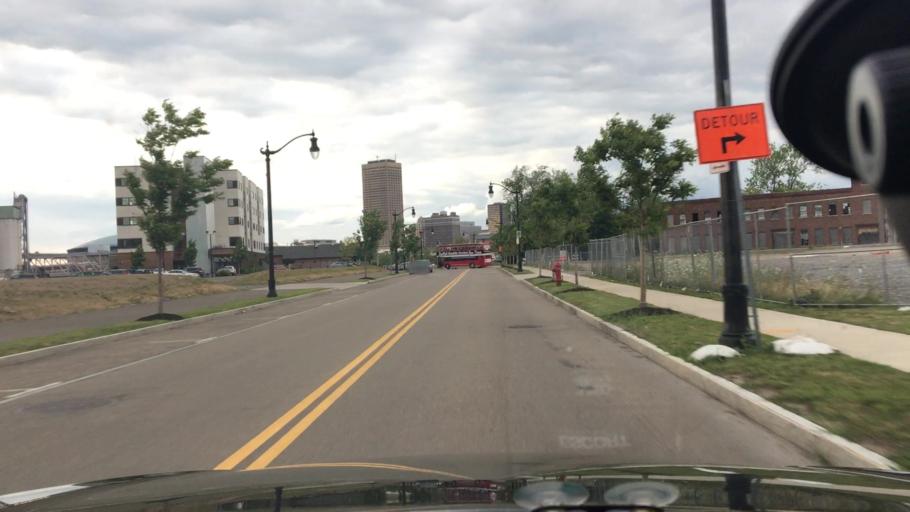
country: US
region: New York
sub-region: Erie County
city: Buffalo
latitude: 42.8682
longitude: -78.8686
